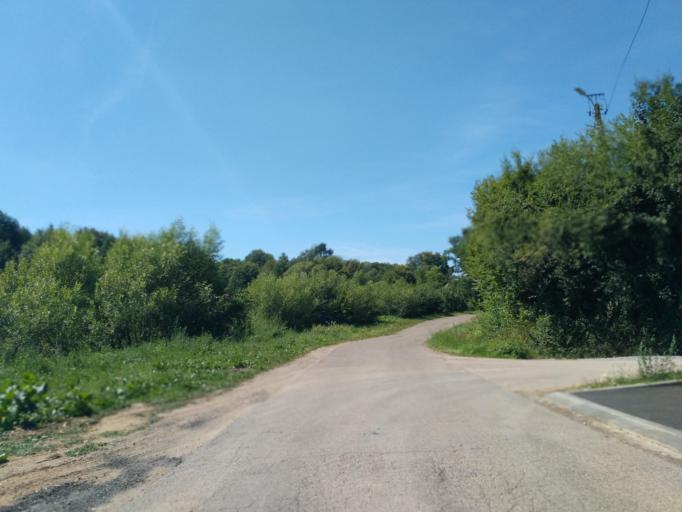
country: PL
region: Subcarpathian Voivodeship
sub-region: Powiat sanocki
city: Nowosielce-Gniewosz
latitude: 49.5388
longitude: 22.0566
